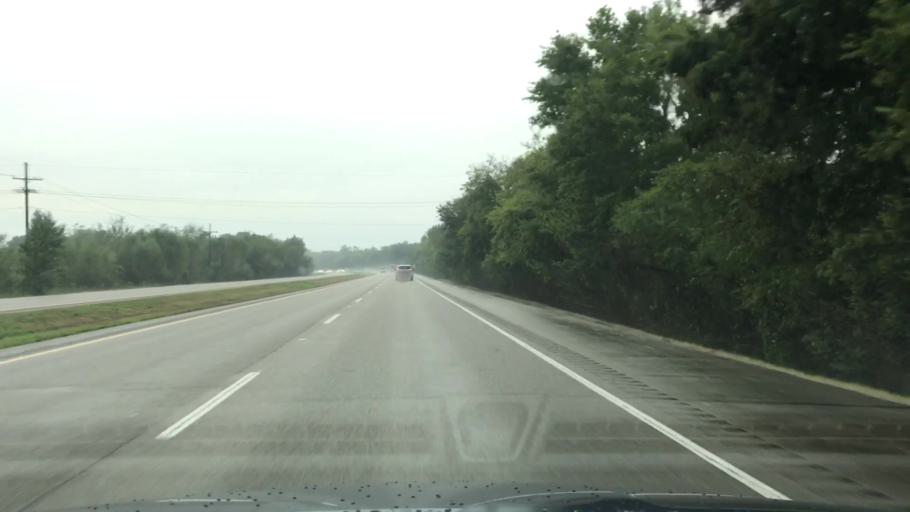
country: US
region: Louisiana
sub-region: Saint Charles Parish
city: Paradis
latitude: 29.8586
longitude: -90.4470
